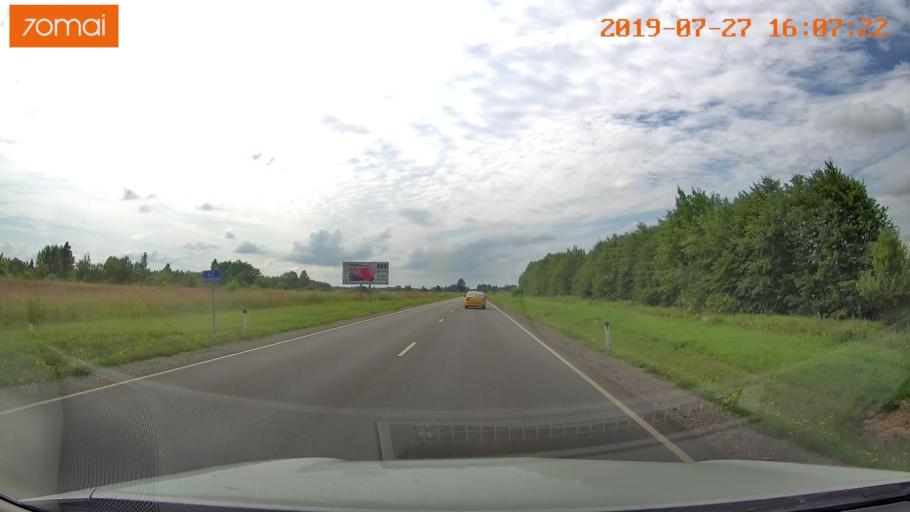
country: RU
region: Kaliningrad
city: Chernyakhovsk
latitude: 54.6352
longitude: 21.7588
